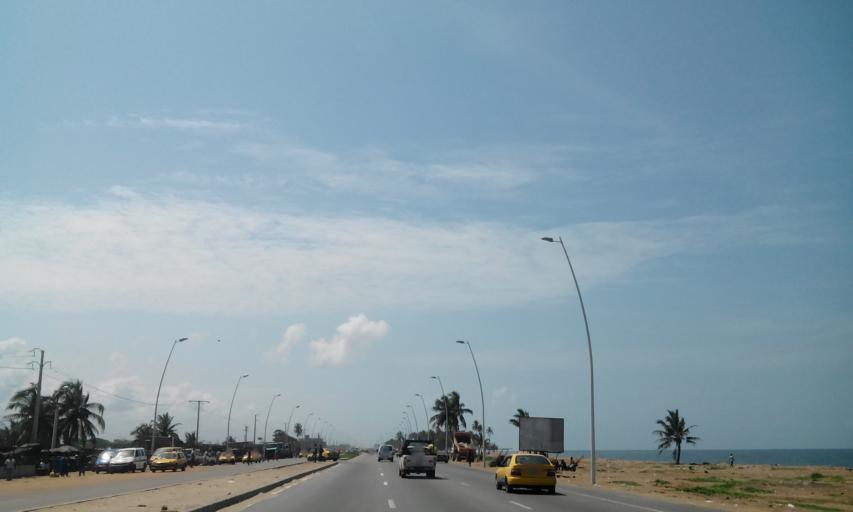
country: CI
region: Lagunes
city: Bingerville
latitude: 5.2399
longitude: -3.9011
